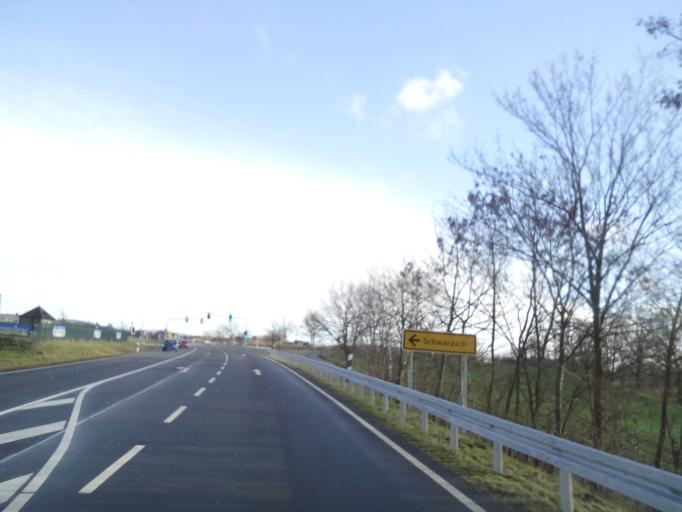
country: DE
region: Bavaria
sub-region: Upper Franconia
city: Mainleus
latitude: 50.1065
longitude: 11.3621
